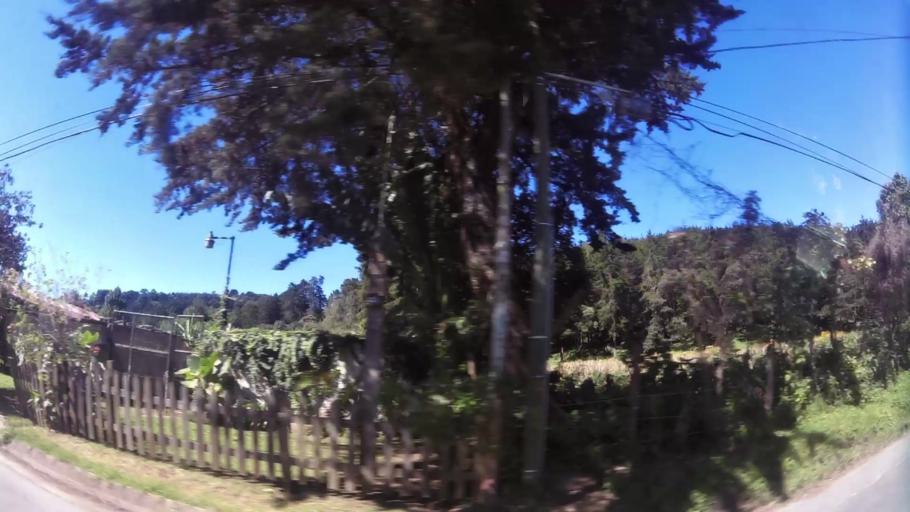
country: GT
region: Guatemala
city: San Jose Pinula
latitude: 14.5328
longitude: -90.4151
